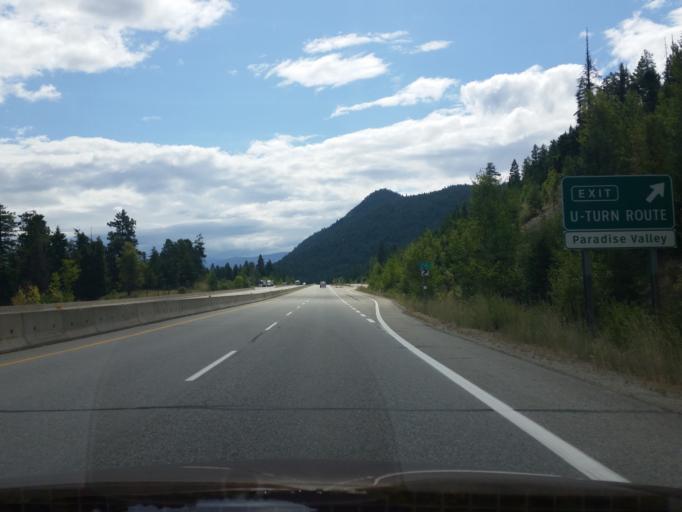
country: CA
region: British Columbia
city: Peachland
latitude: 49.8252
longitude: -119.7918
